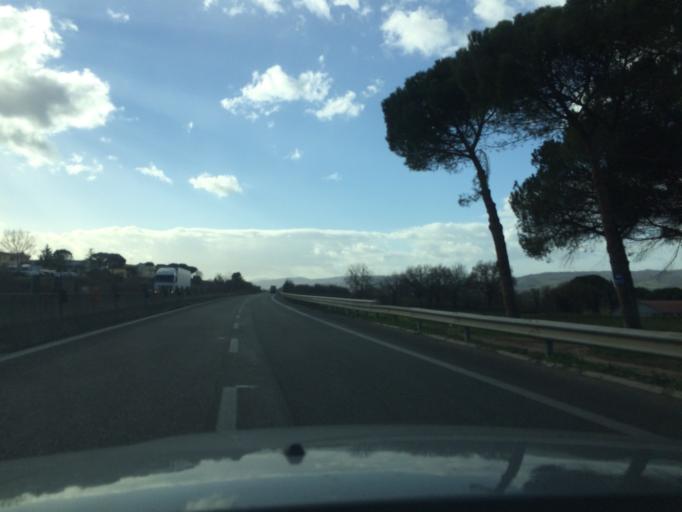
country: IT
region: Umbria
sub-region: Provincia di Perugia
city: Collepepe
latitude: 42.9084
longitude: 12.3918
